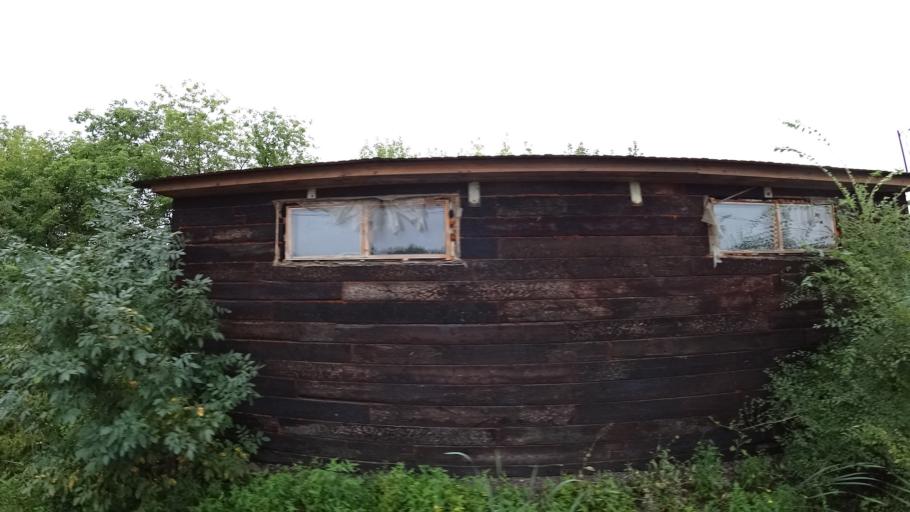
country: RU
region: Primorskiy
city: Monastyrishche
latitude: 44.2023
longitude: 132.4254
